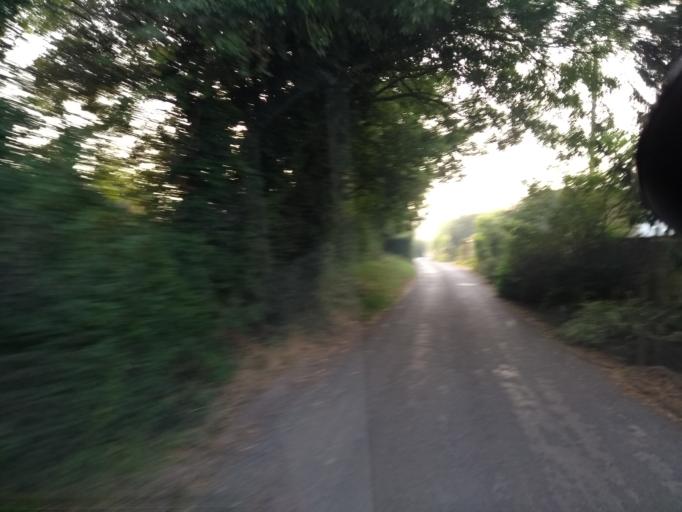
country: GB
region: England
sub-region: Somerset
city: Ilminster
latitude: 50.9867
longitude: -2.9552
